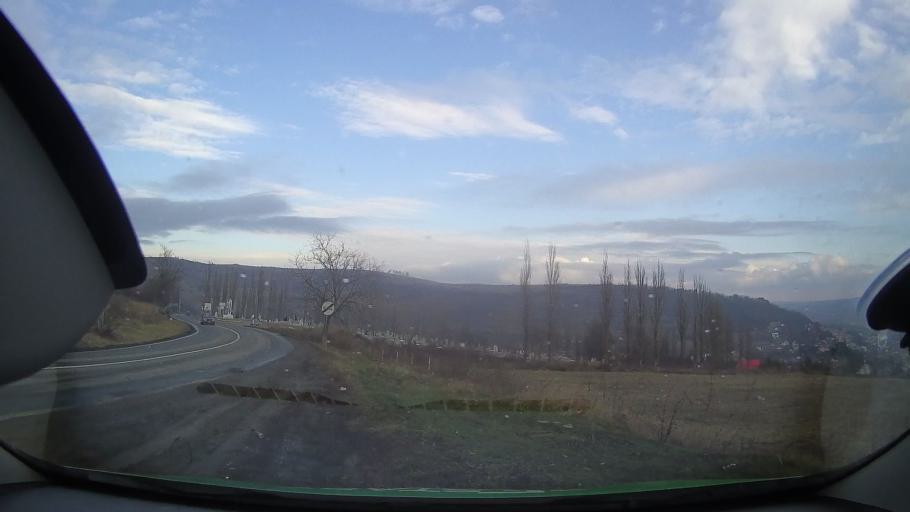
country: RO
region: Mures
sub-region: Municipiul Tarnaveni
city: Tarnaveni
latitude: 46.3357
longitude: 24.2793
